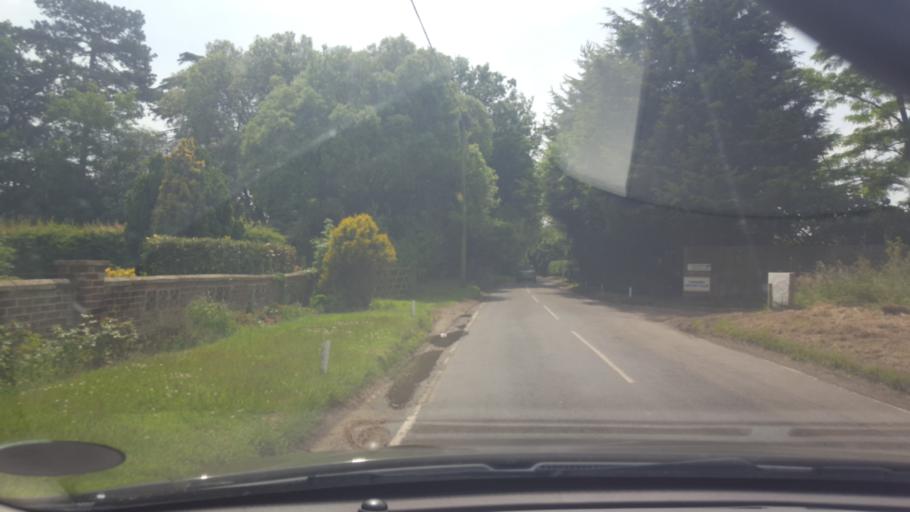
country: GB
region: England
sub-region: Essex
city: Little Clacton
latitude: 51.8707
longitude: 1.1244
